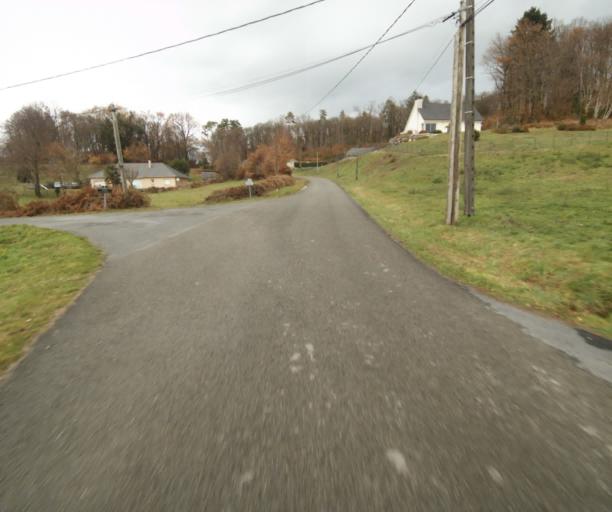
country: FR
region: Limousin
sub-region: Departement de la Correze
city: Saint-Mexant
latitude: 45.2875
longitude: 1.6340
